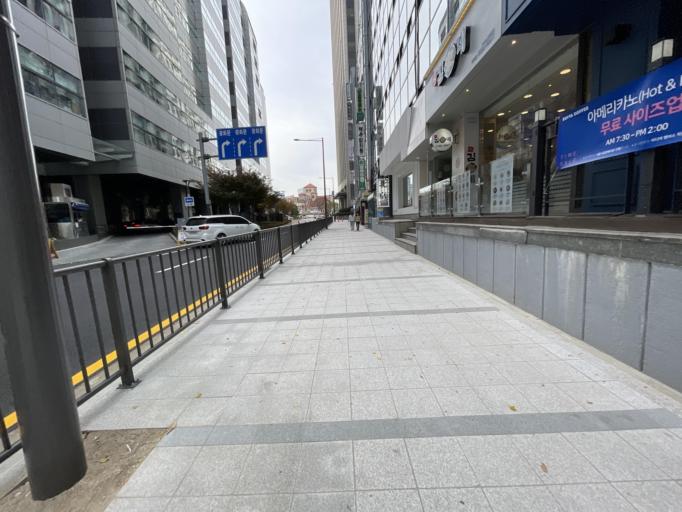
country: KR
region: Seoul
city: Seoul
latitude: 37.5670
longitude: 126.9790
